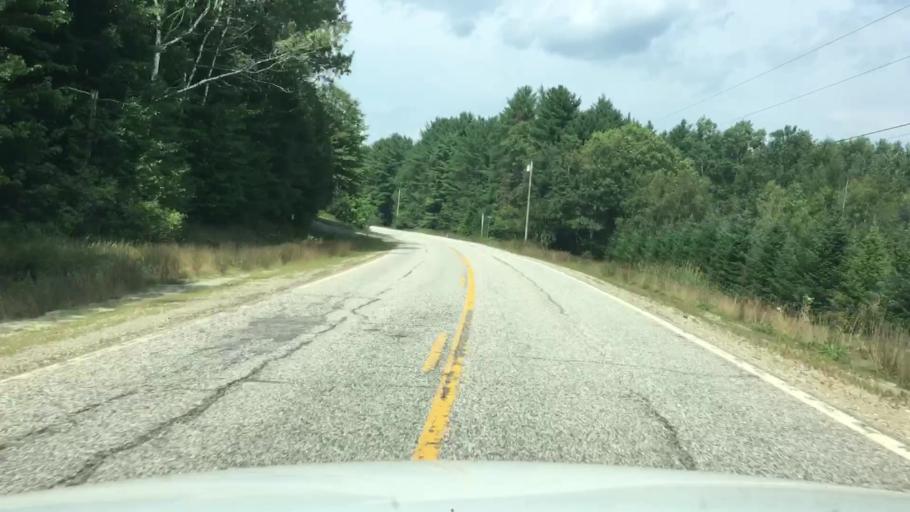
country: US
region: Maine
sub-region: Oxford County
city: Rumford
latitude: 44.5662
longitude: -70.7159
